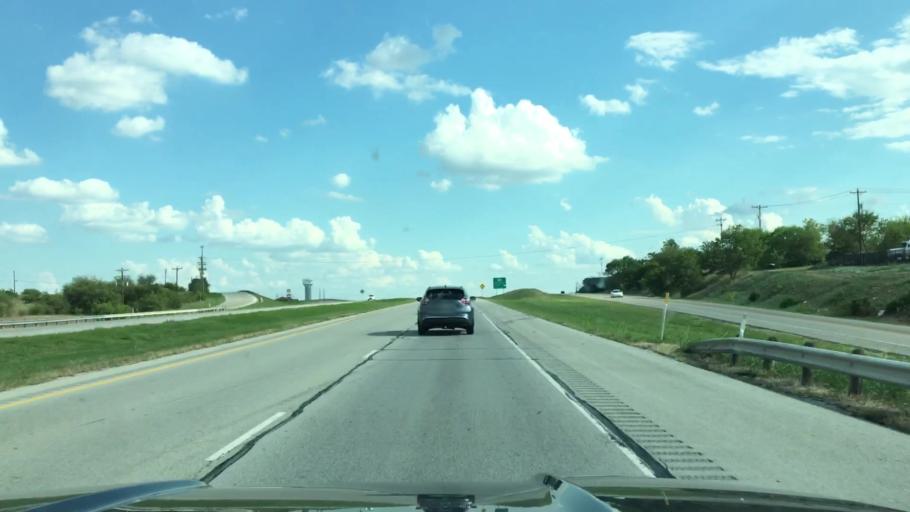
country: US
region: Texas
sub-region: Tarrant County
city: Pecan Acres
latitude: 32.9775
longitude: -97.4242
